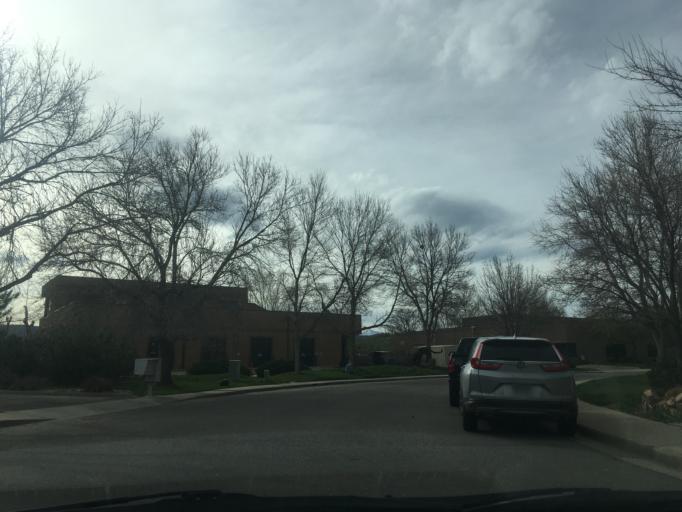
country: US
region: Colorado
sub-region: Boulder County
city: Boulder
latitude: 40.0299
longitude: -105.2279
